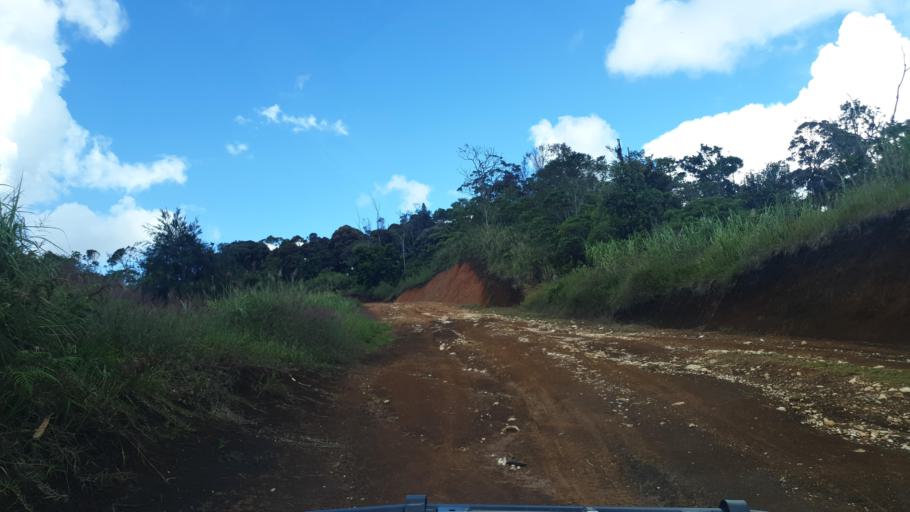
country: PG
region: Eastern Highlands
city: Goroka
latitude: -6.2794
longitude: 145.1923
